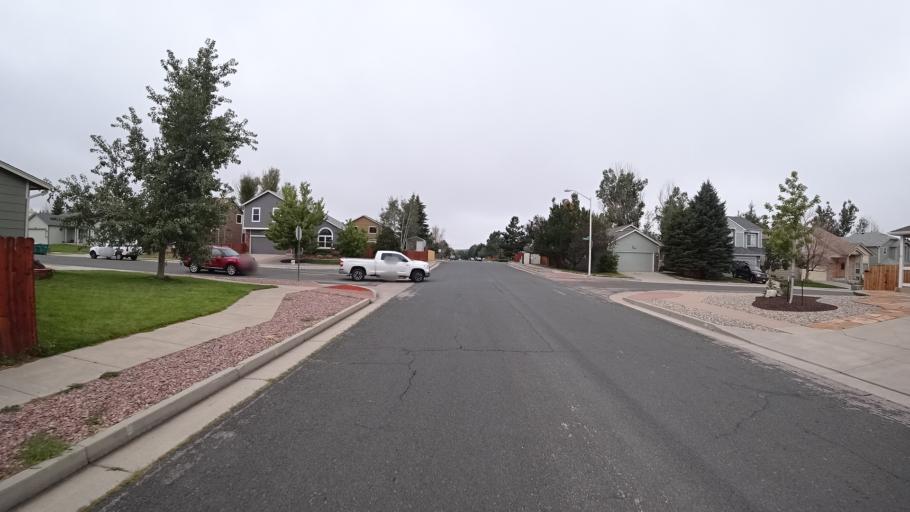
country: US
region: Colorado
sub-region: El Paso County
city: Cimarron Hills
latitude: 38.9227
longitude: -104.7244
